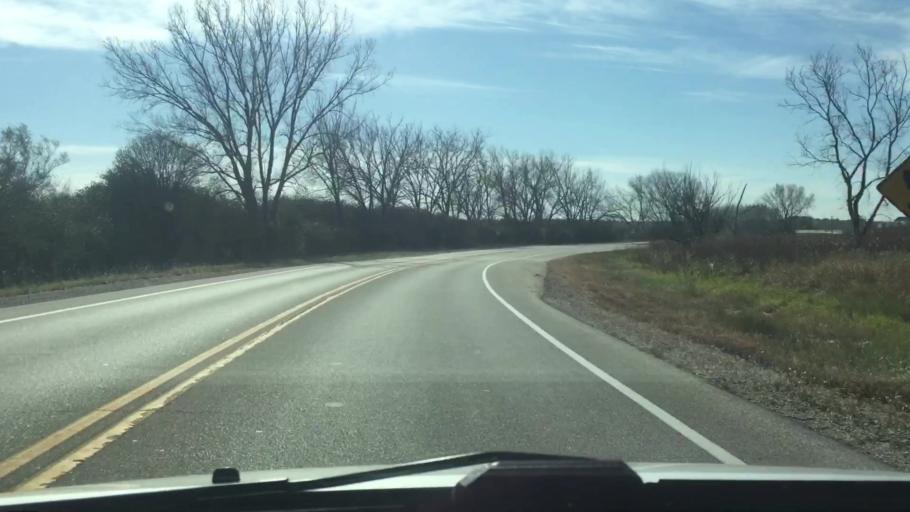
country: US
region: Wisconsin
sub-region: Waukesha County
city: Pewaukee
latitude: 43.0535
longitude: -88.2521
